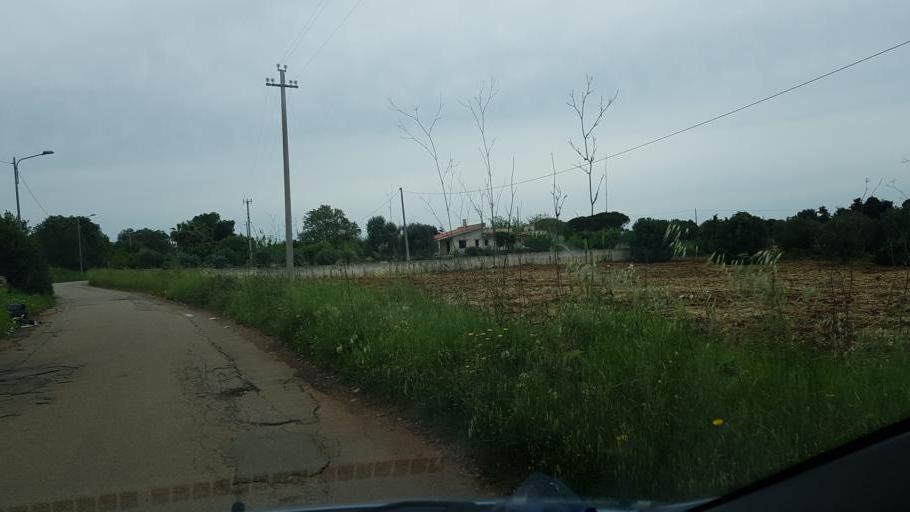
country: IT
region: Apulia
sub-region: Provincia di Brindisi
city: San Vito dei Normanni
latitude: 40.6640
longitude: 17.7306
